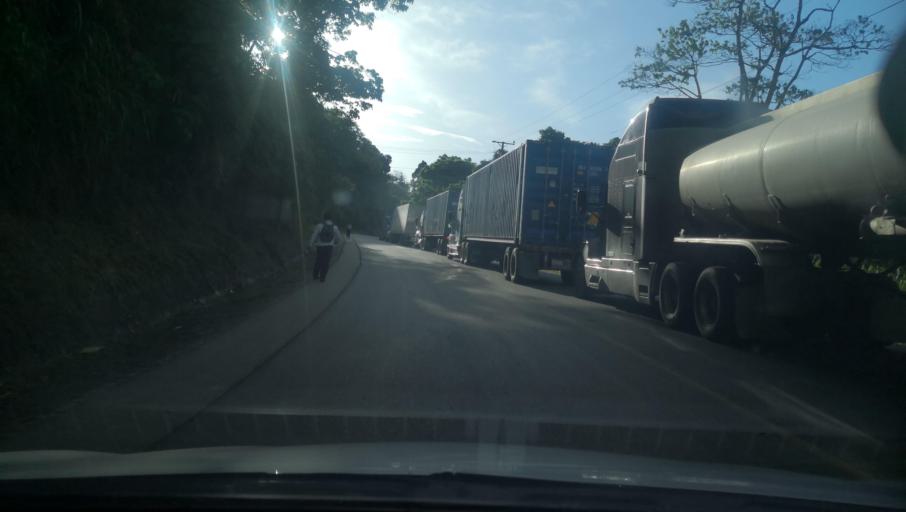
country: HN
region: El Paraiso
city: El Paraiso
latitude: 13.7894
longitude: -86.5651
